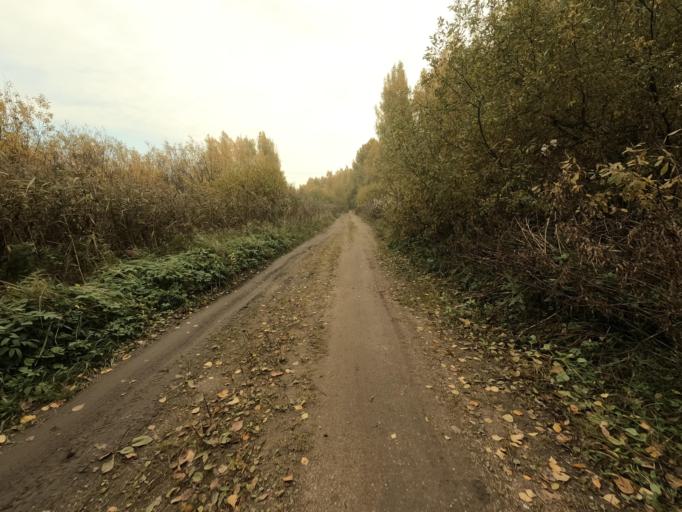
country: RU
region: Novgorod
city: Pankovka
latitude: 58.8725
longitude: 30.8905
